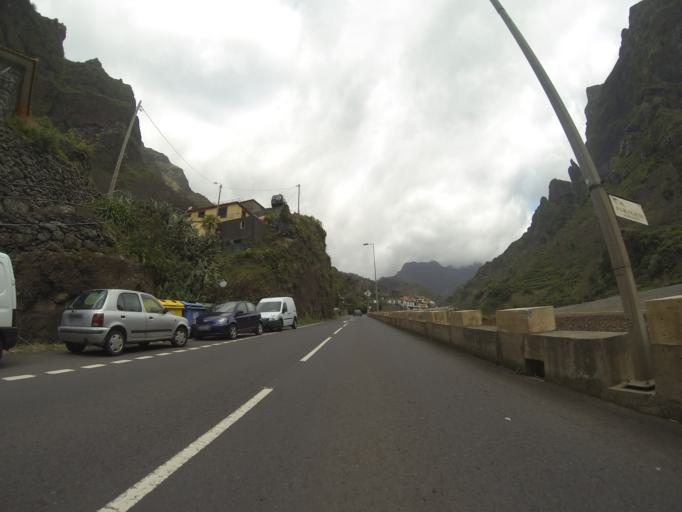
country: PT
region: Madeira
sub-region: Ribeira Brava
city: Campanario
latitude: 32.7187
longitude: -17.0320
